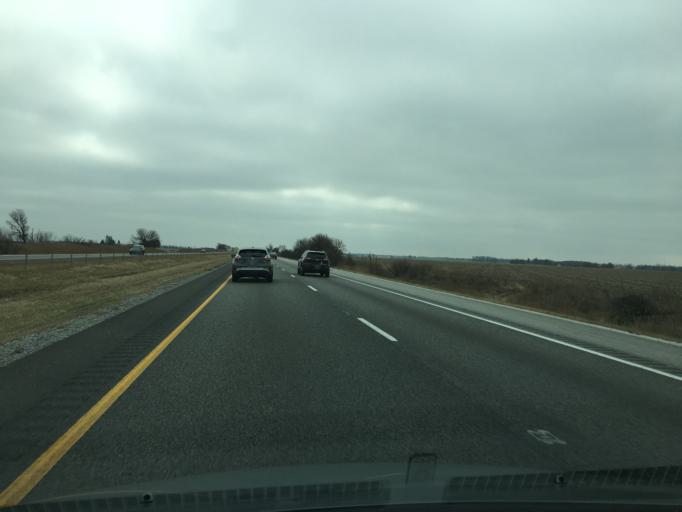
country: US
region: Indiana
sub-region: Jasper County
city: Remington
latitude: 40.8339
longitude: -87.1711
